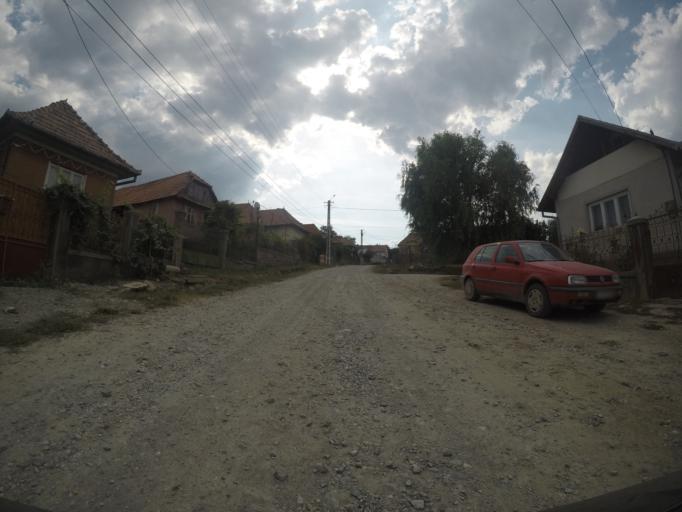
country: RO
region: Cluj
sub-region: Comuna Sandulesti
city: Sandulesti
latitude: 46.5798
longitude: 23.7152
